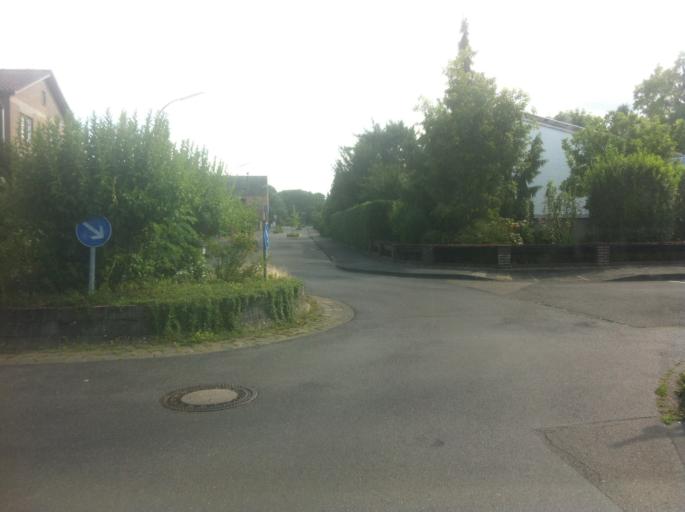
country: DE
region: North Rhine-Westphalia
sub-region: Regierungsbezirk Koln
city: Erftstadt
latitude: 50.8024
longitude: 6.7613
